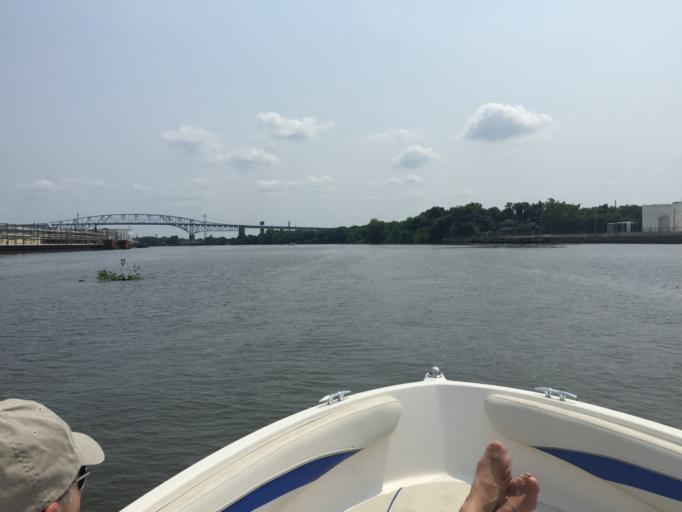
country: US
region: Pennsylvania
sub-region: Delaware County
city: Colwyn
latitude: 39.9077
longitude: -75.2157
